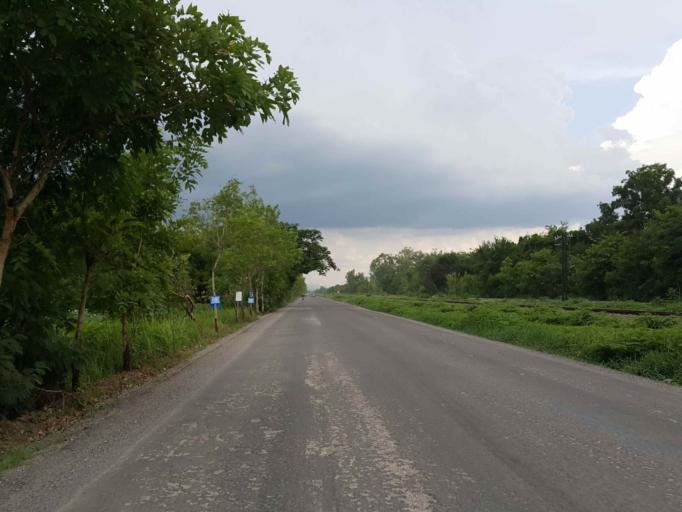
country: TH
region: Chiang Mai
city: Saraphi
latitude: 18.7297
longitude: 99.0335
